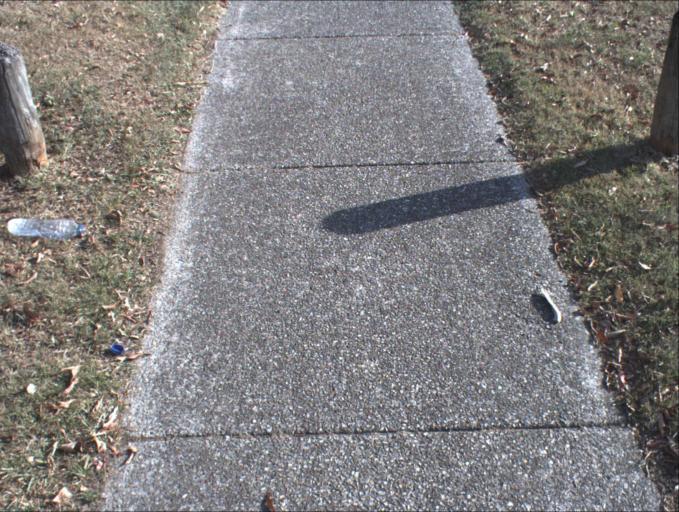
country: AU
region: Queensland
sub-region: Logan
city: Beenleigh
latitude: -27.6975
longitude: 153.1858
